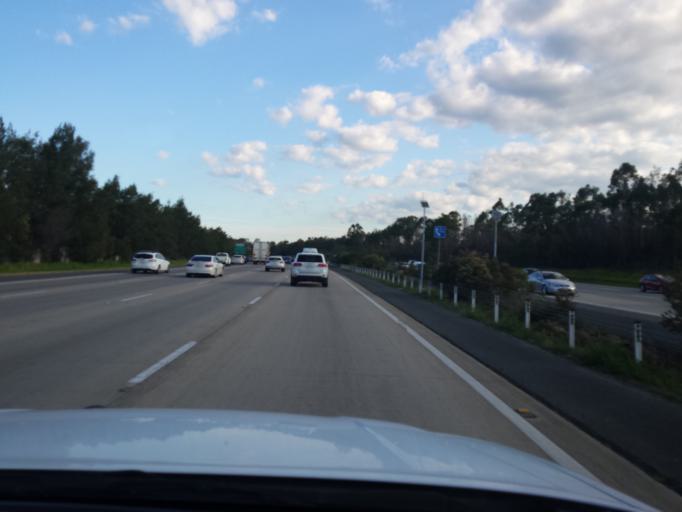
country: AU
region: Queensland
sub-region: Gold Coast
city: Ormeau Hills
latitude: -27.7757
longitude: 153.2521
